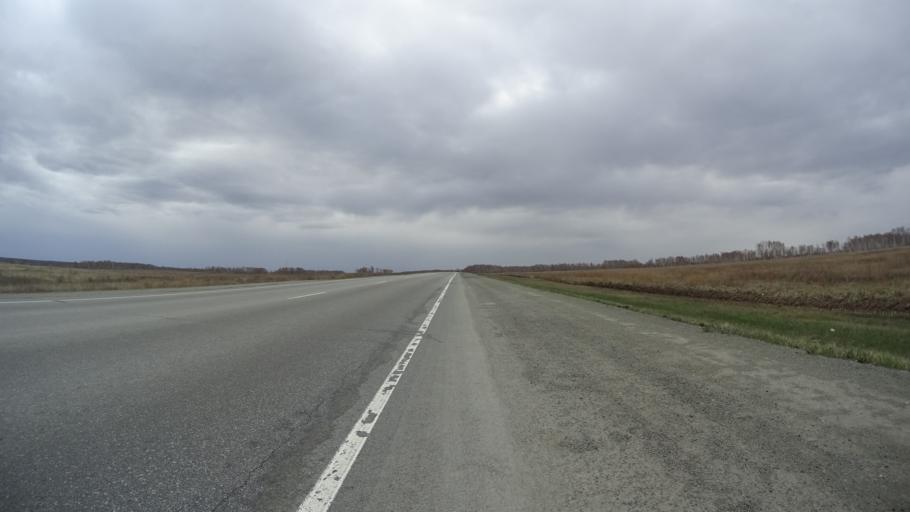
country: RU
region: Chelyabinsk
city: Yemanzhelinsk
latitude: 54.7060
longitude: 61.2566
